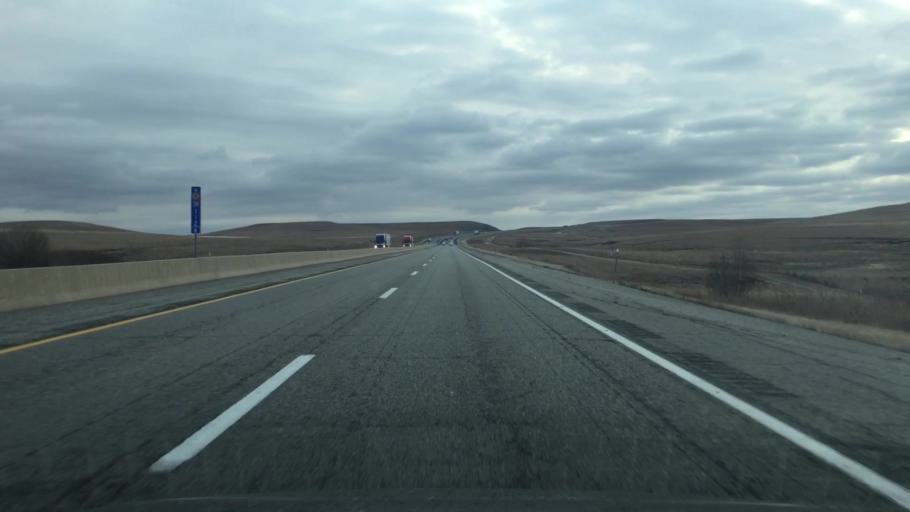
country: US
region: Kansas
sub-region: Chase County
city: Cottonwood Falls
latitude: 38.2504
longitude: -96.3933
